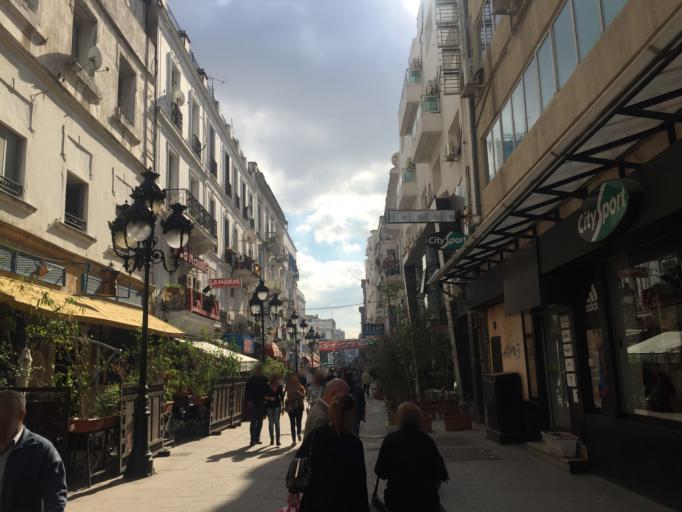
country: TN
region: Tunis
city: Tunis
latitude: 36.8012
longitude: 10.1822
